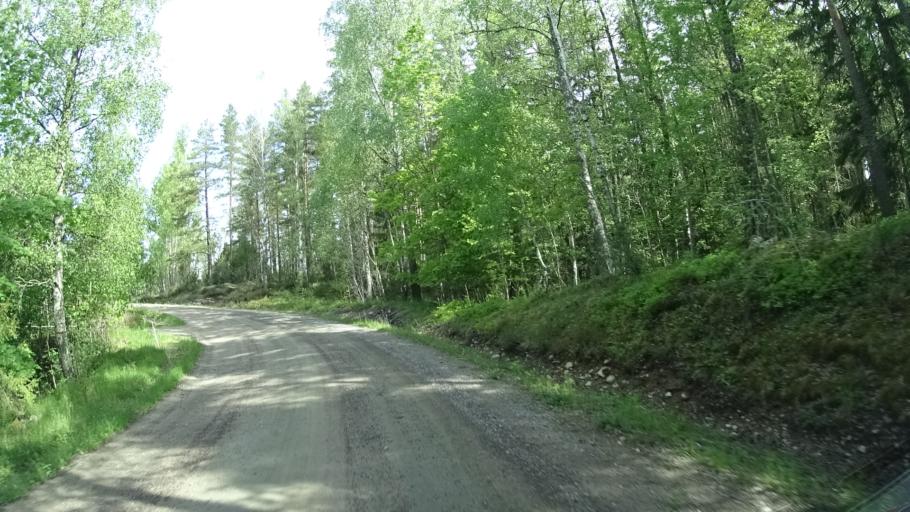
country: SE
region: OEstergoetland
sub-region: Finspangs Kommun
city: Finspang
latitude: 58.7521
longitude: 15.8301
